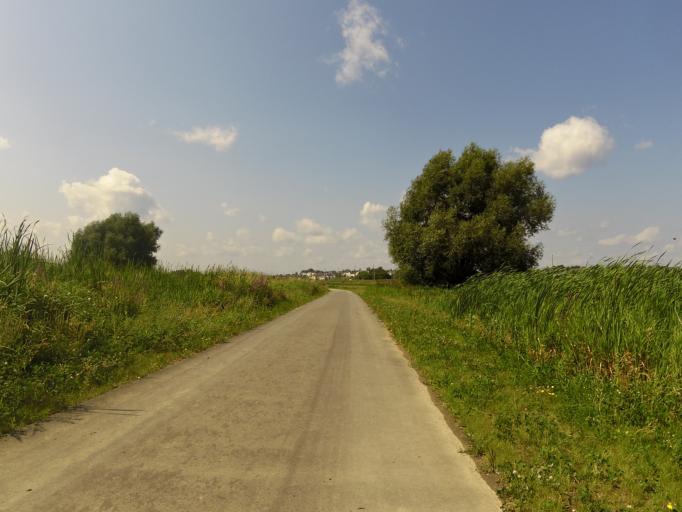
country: CA
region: Ontario
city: Bells Corners
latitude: 45.3063
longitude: -75.9259
